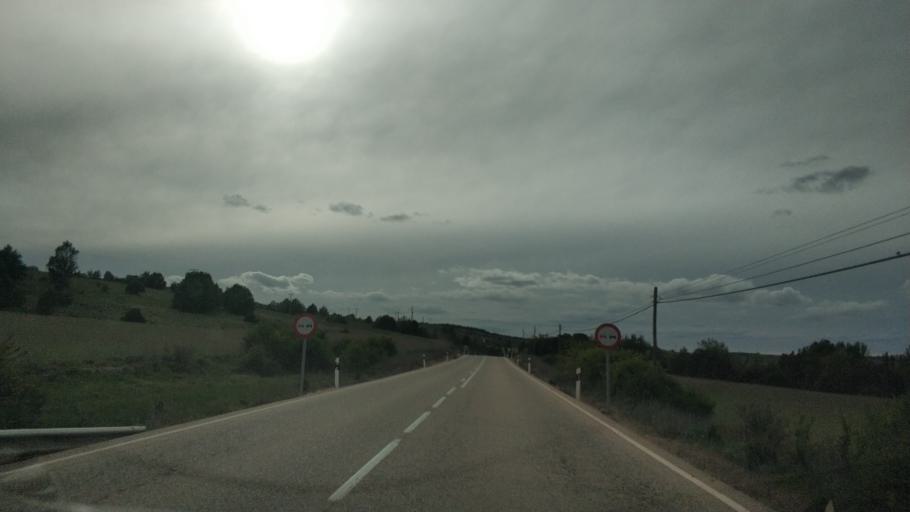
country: ES
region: Castille and Leon
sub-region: Provincia de Soria
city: El Burgo de Osma
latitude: 41.5772
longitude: -3.0300
